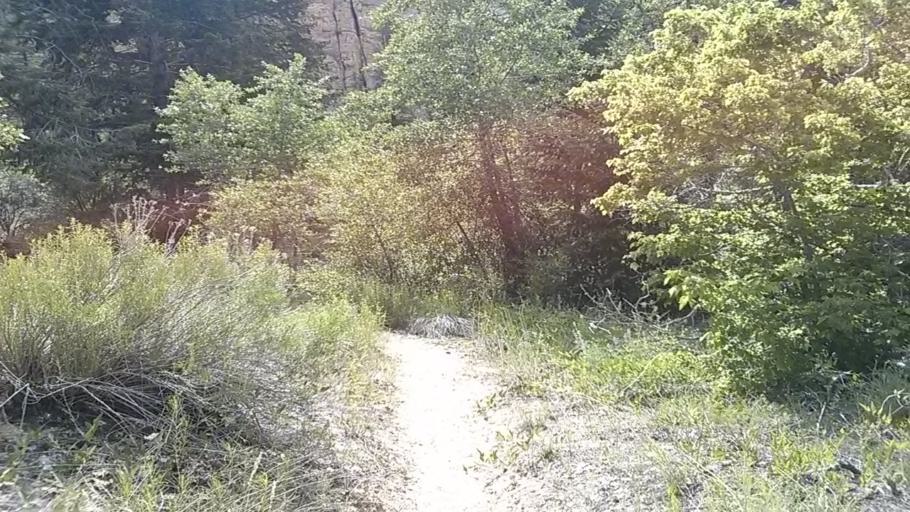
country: US
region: Utah
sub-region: Wayne County
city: Loa
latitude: 37.8897
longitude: -111.6362
